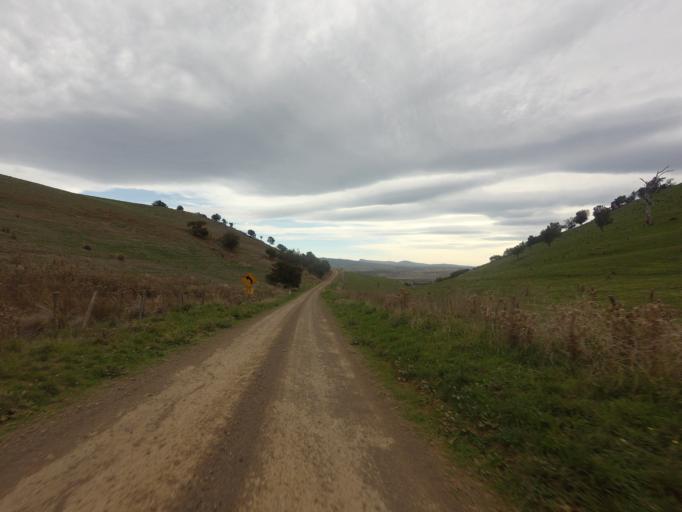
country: AU
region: Tasmania
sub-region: Derwent Valley
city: New Norfolk
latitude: -42.4541
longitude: 146.7679
